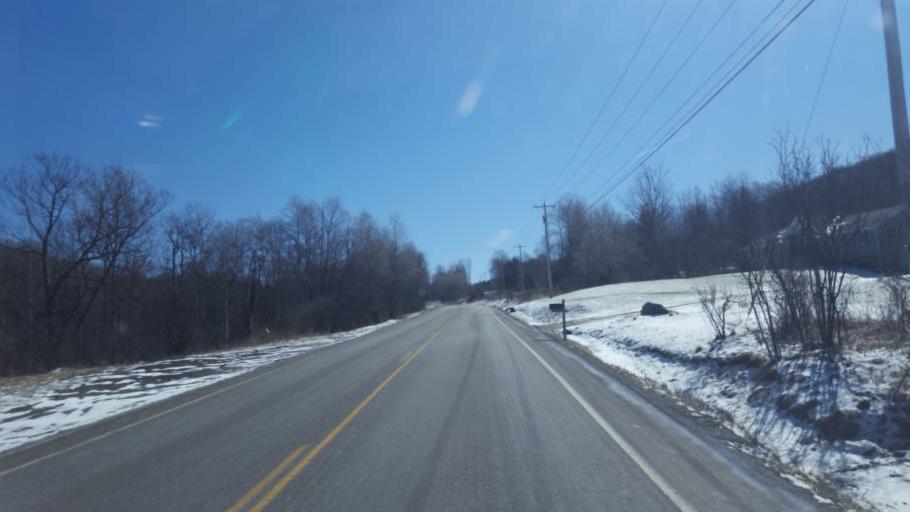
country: US
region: New York
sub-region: Allegany County
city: Andover
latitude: 42.0729
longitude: -77.8477
